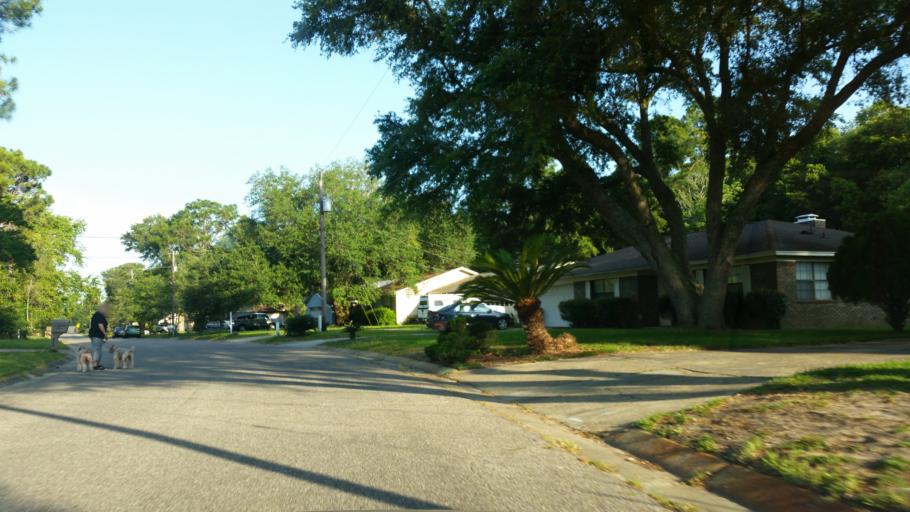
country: US
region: Florida
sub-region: Escambia County
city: Ferry Pass
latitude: 30.5059
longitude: -87.1990
